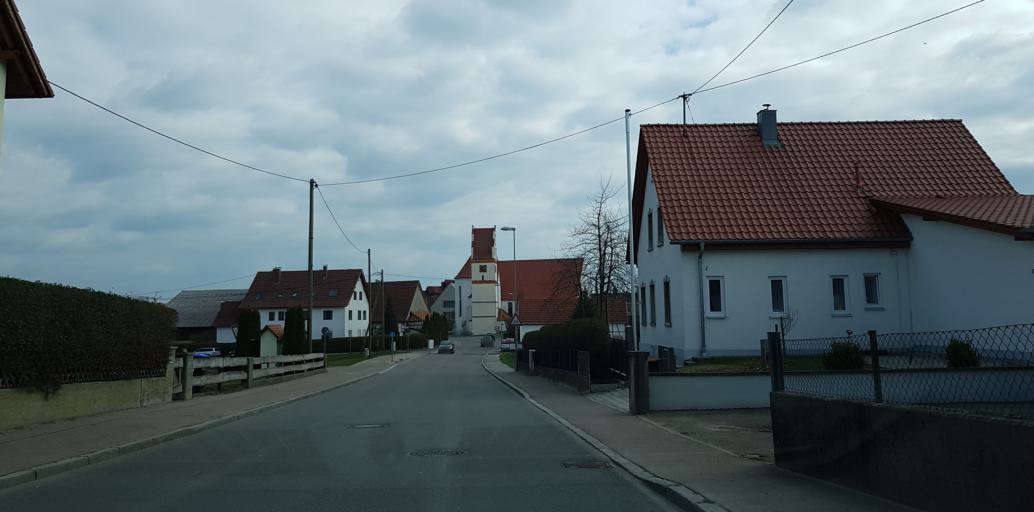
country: DE
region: Baden-Wuerttemberg
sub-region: Tuebingen Region
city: Erbach
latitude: 48.3551
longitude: 9.8945
